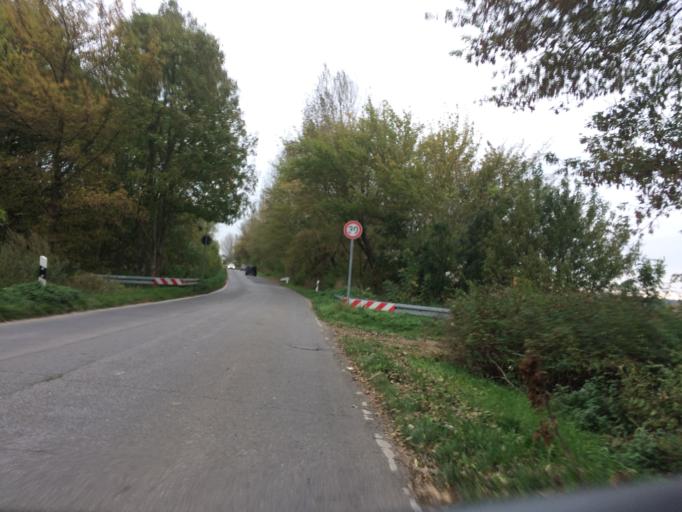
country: DE
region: Berlin
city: Blankenfelde
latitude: 52.6118
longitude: 13.4096
